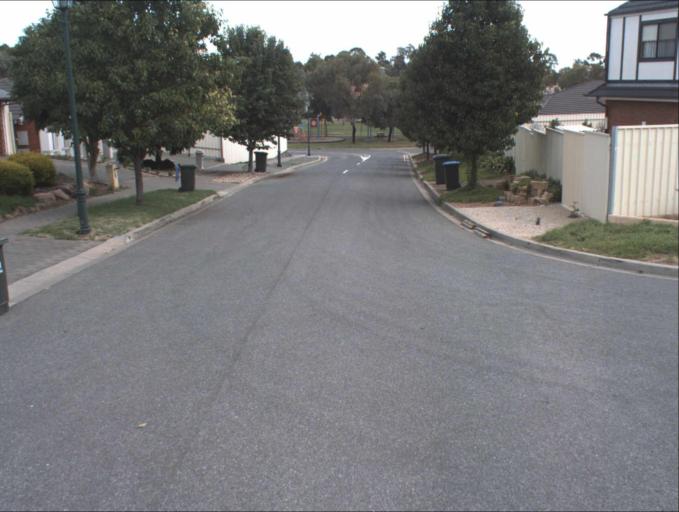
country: AU
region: South Australia
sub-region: Port Adelaide Enfield
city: Gilles Plains
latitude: -34.8449
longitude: 138.6468
